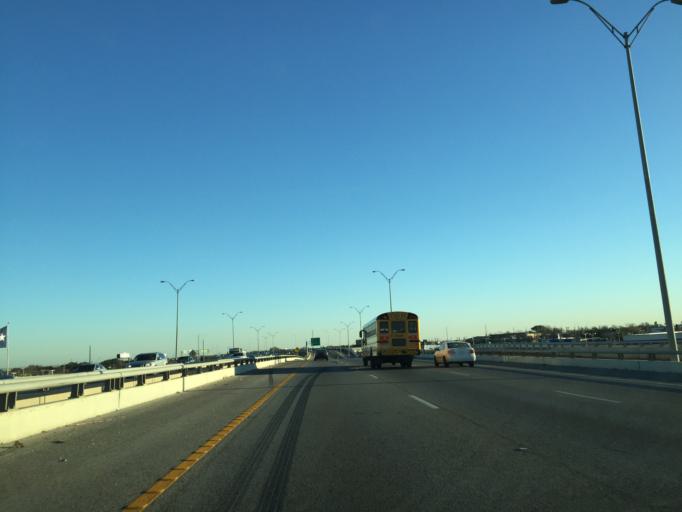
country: US
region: Texas
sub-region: Travis County
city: Austin
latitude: 30.3529
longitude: -97.7145
